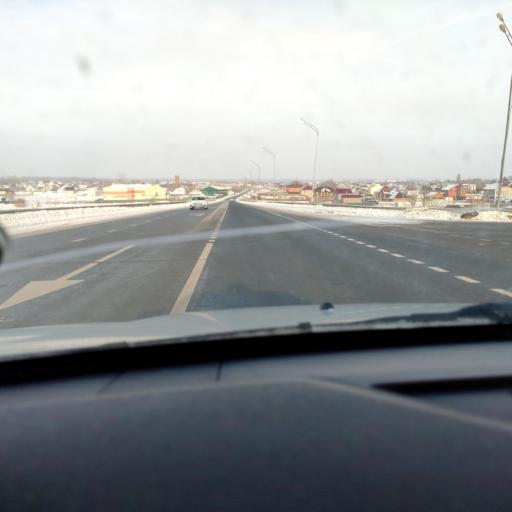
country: RU
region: Samara
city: Smyshlyayevka
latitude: 53.1518
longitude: 50.3836
